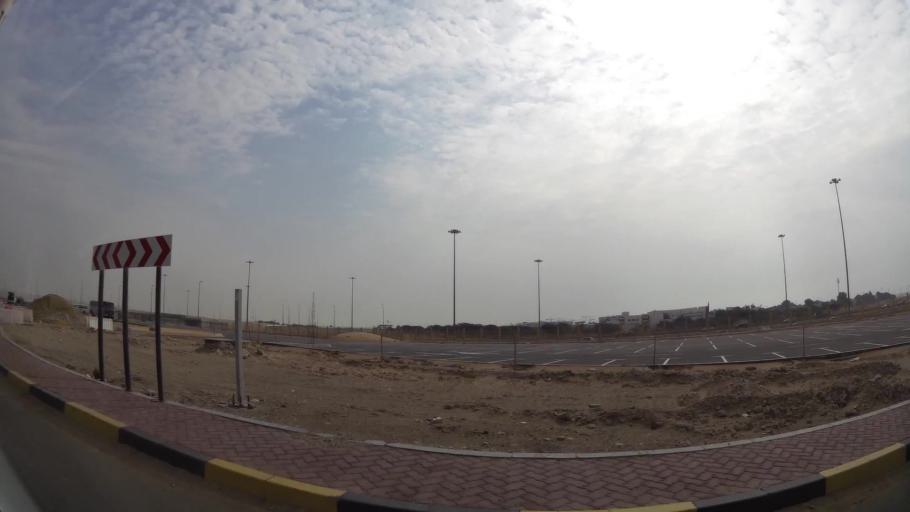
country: AE
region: Abu Dhabi
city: Abu Dhabi
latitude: 24.6838
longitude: 54.7697
